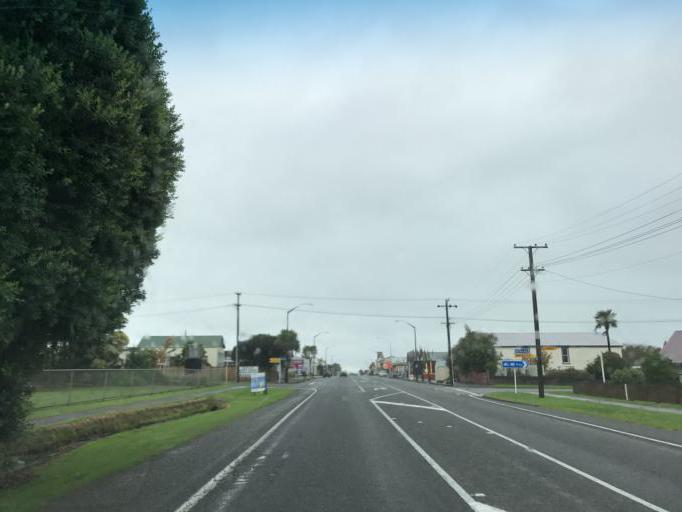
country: NZ
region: Taranaki
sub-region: South Taranaki District
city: Patea
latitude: -39.7643
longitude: 174.6297
